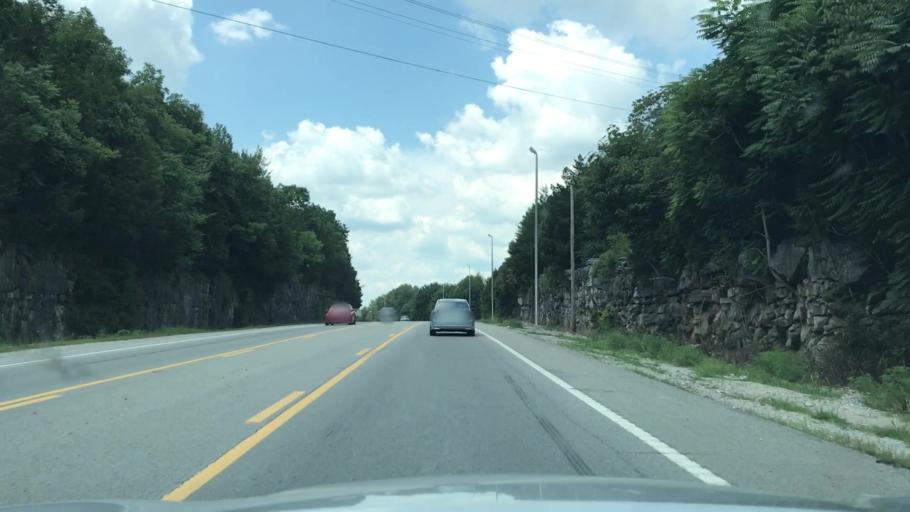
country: US
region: Tennessee
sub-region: Overton County
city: Livingston
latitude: 36.3980
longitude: -85.3059
